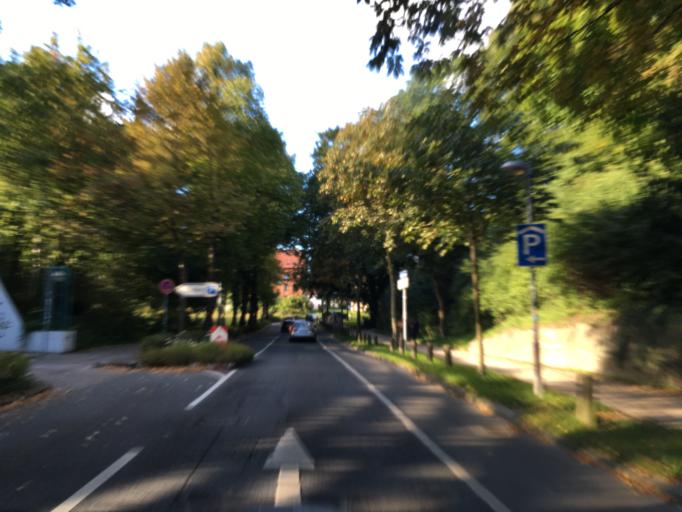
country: DE
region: Lower Saxony
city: Lueneburg
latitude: 53.2513
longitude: 10.4031
